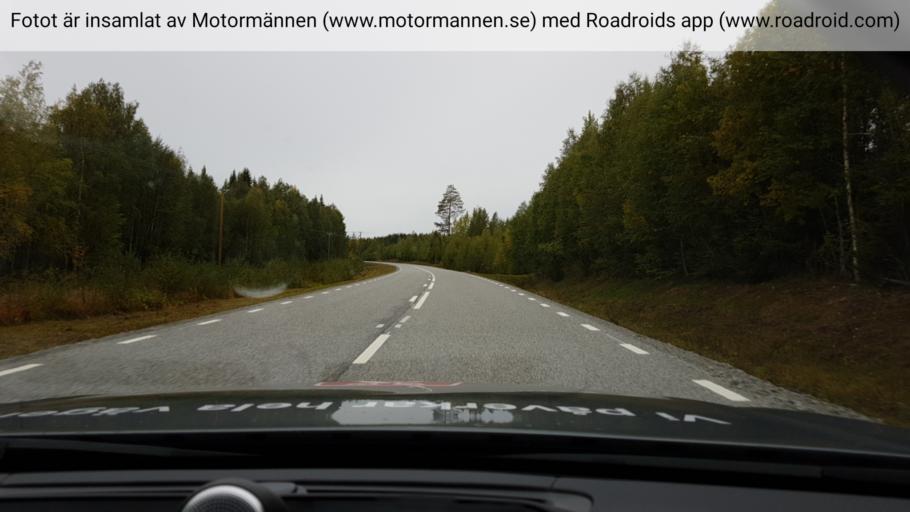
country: SE
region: Jaemtland
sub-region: Stroemsunds Kommun
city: Stroemsund
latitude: 64.1951
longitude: 15.6265
